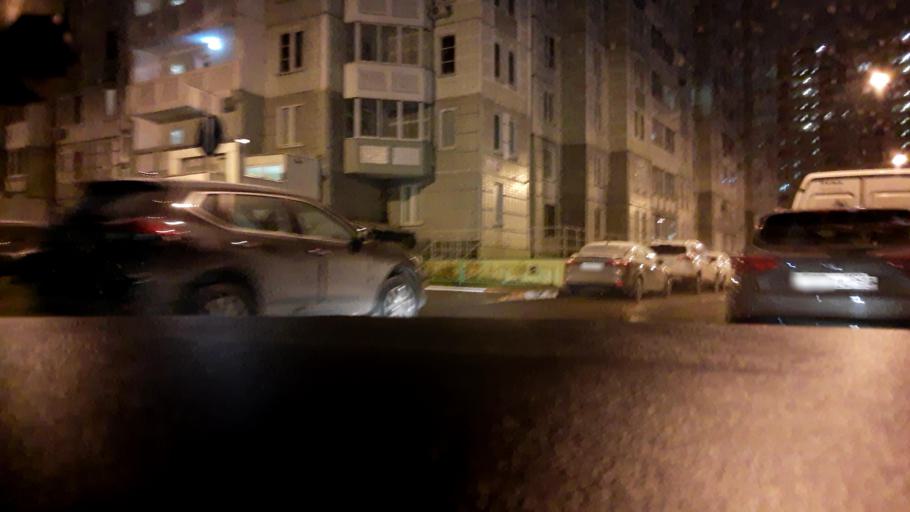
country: RU
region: Moskovskaya
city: Zheleznodorozhnyy
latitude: 55.7465
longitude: 37.9971
